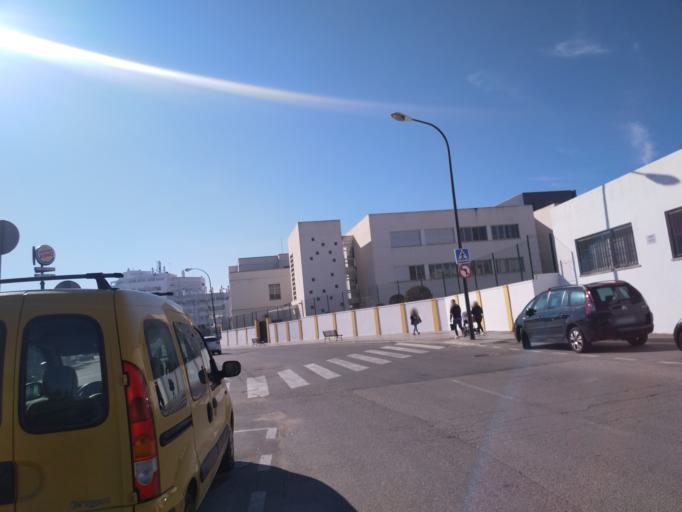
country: ES
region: Andalusia
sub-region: Provincia de Cadiz
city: San Fernando
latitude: 36.4705
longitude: -6.1901
